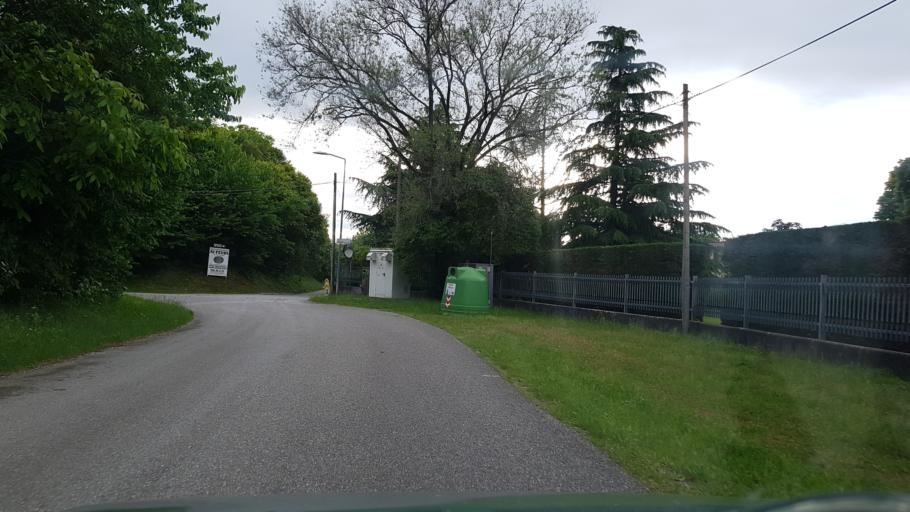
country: IT
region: Friuli Venezia Giulia
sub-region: Provincia di Gorizia
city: Mariano del Friuli
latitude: 45.8937
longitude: 13.4686
